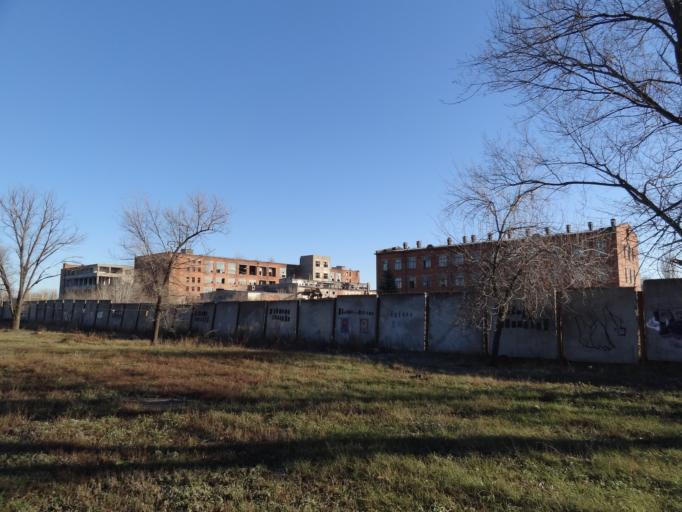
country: RU
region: Saratov
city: Engel's
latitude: 51.4665
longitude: 46.1516
